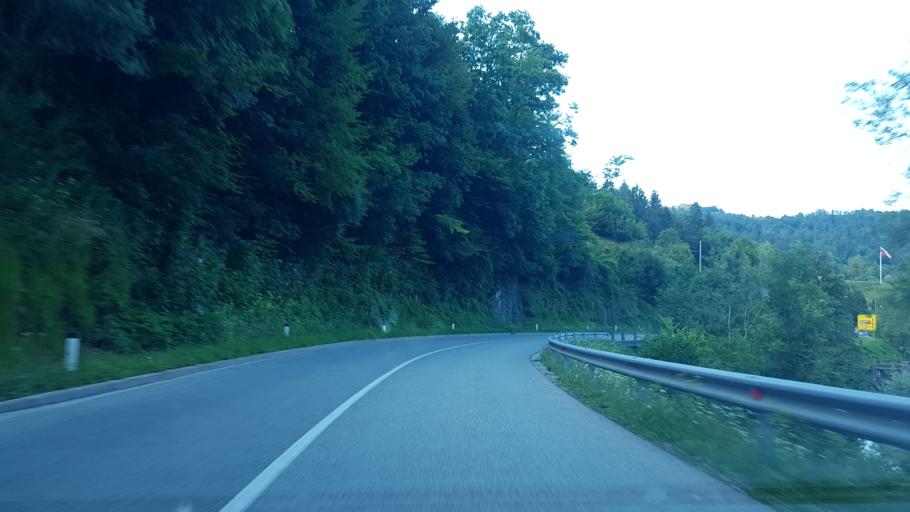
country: SI
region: Gorenja Vas-Poljane
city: Gorenja Vas
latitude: 46.1054
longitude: 14.1146
